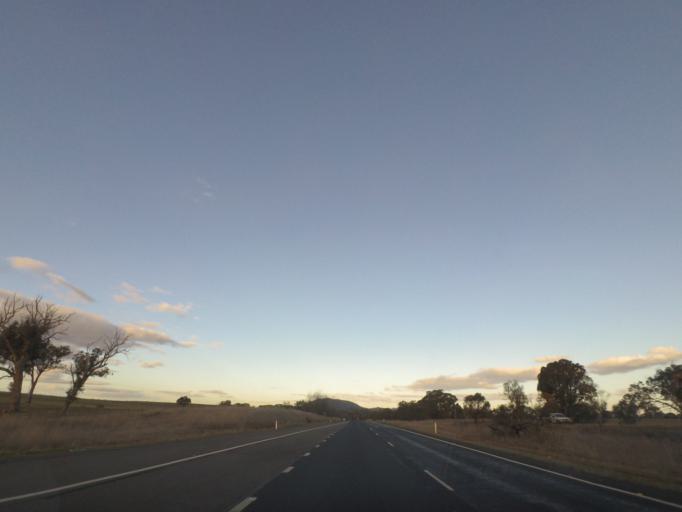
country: AU
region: New South Wales
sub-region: Yass Valley
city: Yass
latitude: -34.7670
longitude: 148.7675
